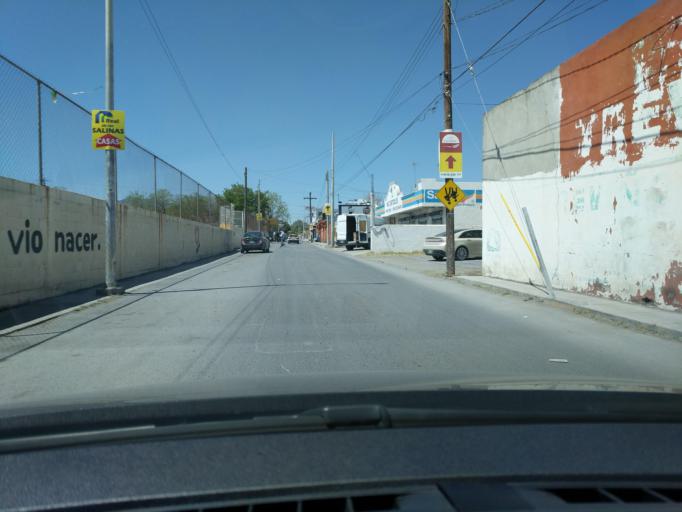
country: MX
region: Nuevo Leon
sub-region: Salinas Victoria
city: Las Torres
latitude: 25.9638
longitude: -100.2942
